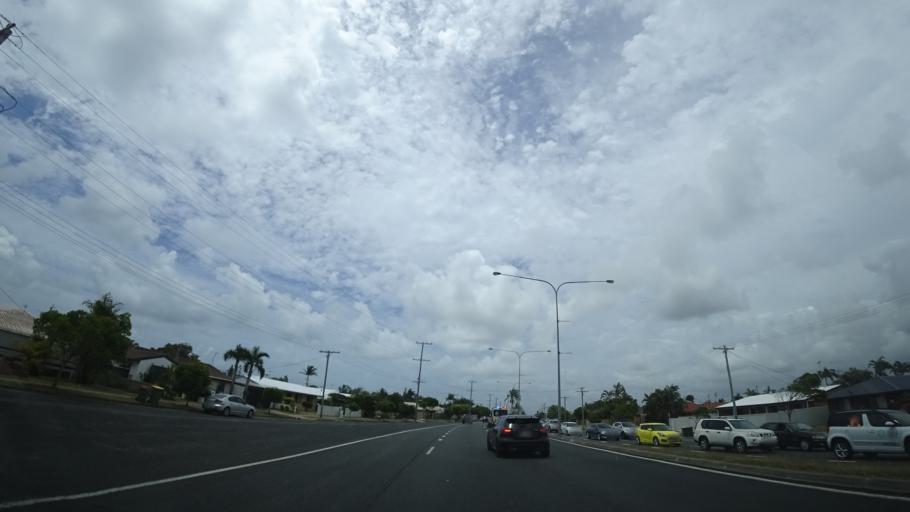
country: AU
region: Queensland
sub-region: Sunshine Coast
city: Mooloolaba
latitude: -26.7061
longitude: 153.1302
